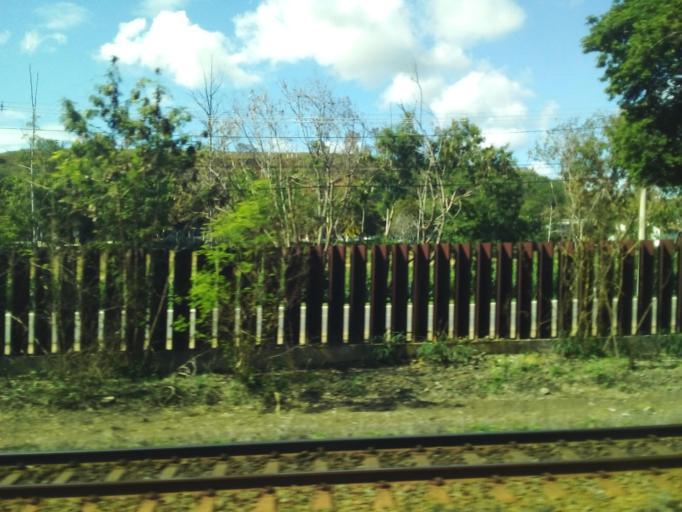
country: BR
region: Minas Gerais
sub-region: Governador Valadares
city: Governador Valadares
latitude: -18.8361
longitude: -41.8891
